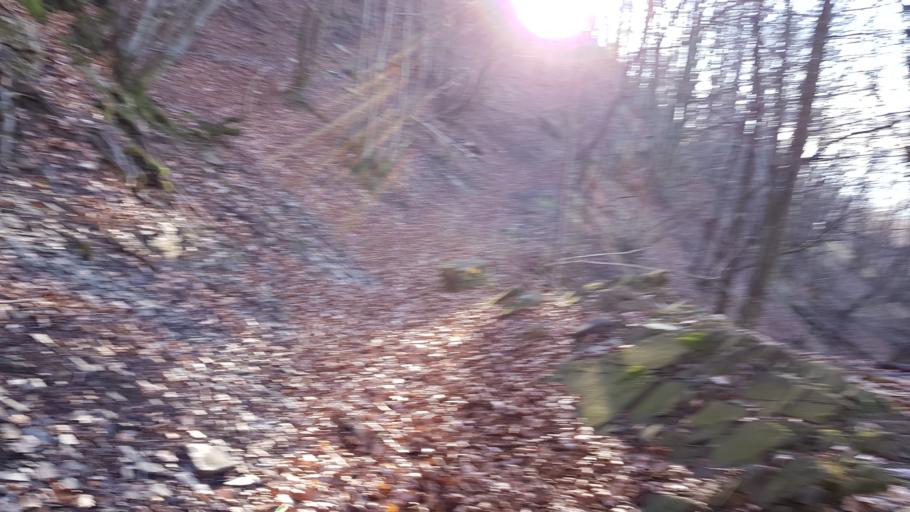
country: IT
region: Liguria
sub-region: Provincia di Genova
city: Torriglia
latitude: 44.5395
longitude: 9.1540
